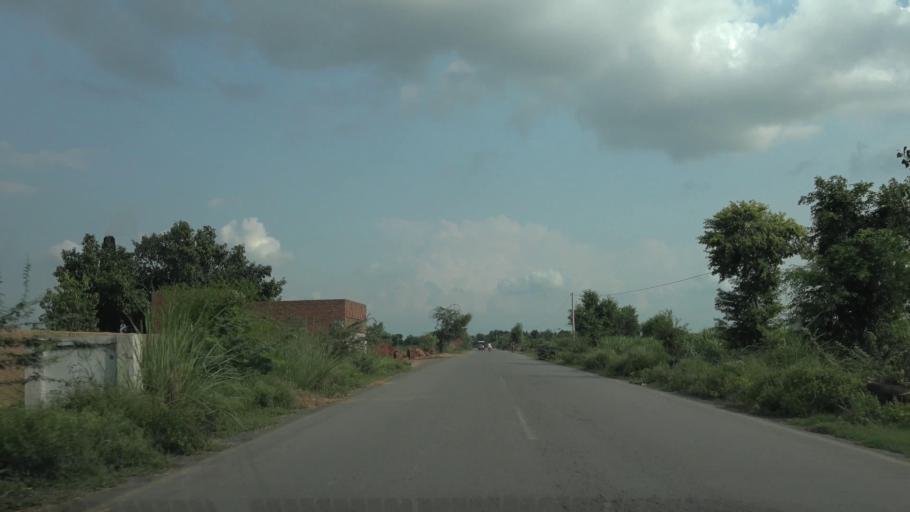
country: PK
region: Punjab
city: Nankana Sahib
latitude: 31.4864
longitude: 73.6091
